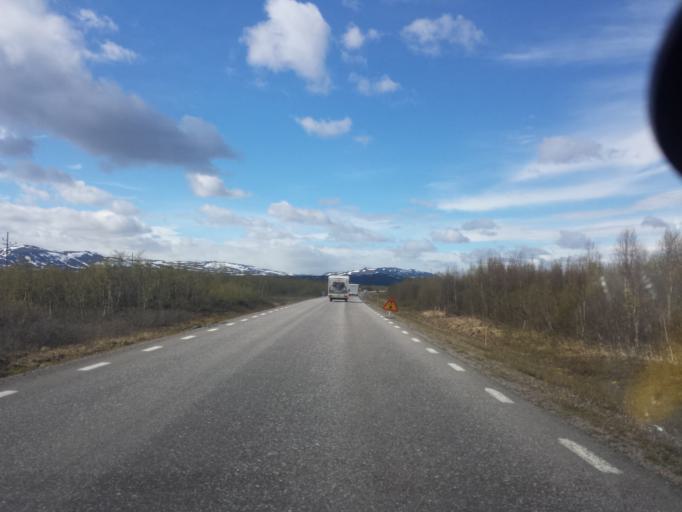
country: SE
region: Norrbotten
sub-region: Kiruna Kommun
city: Kiruna
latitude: 68.0040
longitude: 19.8539
